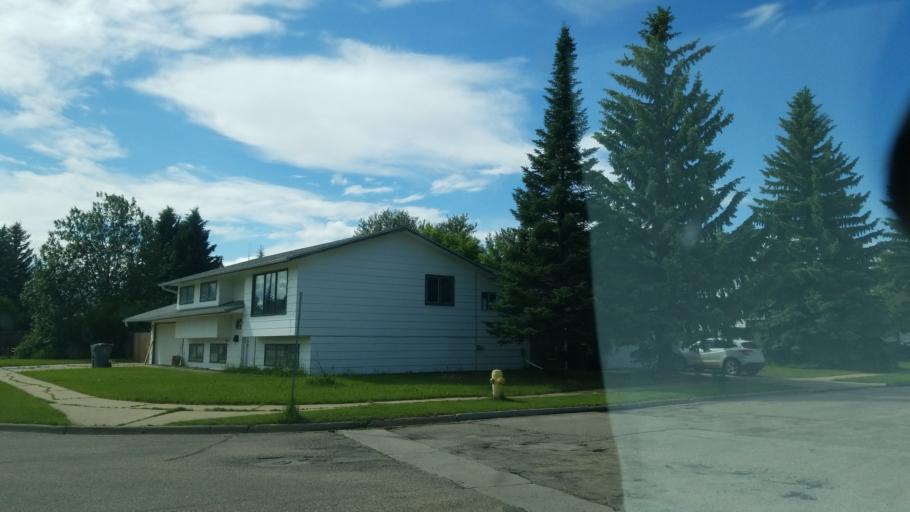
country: CA
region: Saskatchewan
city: Lloydminster
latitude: 53.2670
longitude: -110.0168
